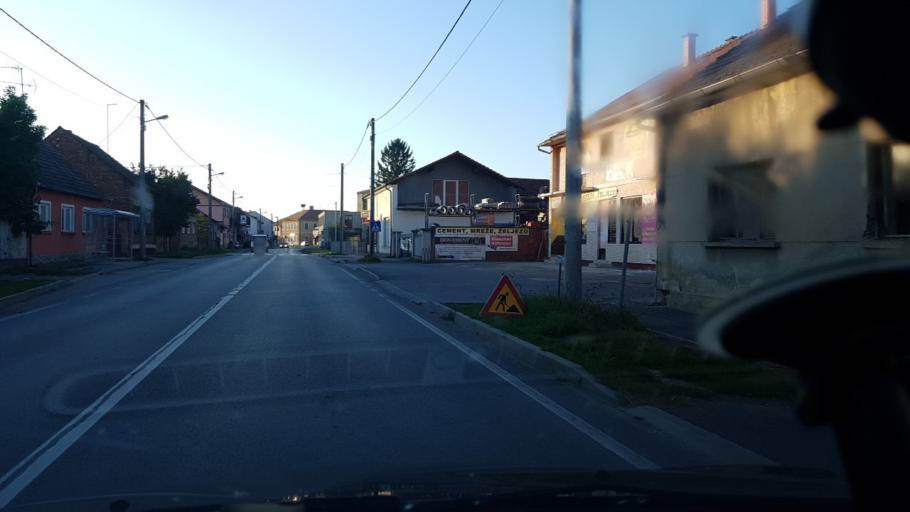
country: HR
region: Koprivnicko-Krizevacka
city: Virje
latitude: 46.0647
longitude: 16.9918
